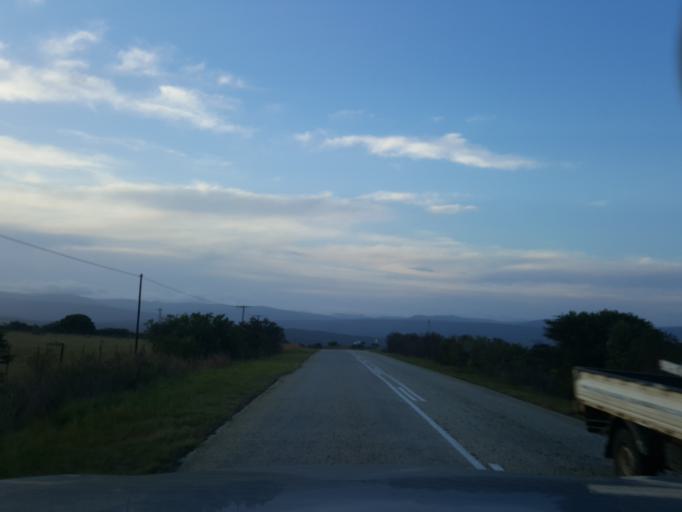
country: ZA
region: Eastern Cape
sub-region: Cacadu District Municipality
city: Grahamstown
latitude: -33.4339
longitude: 26.4829
